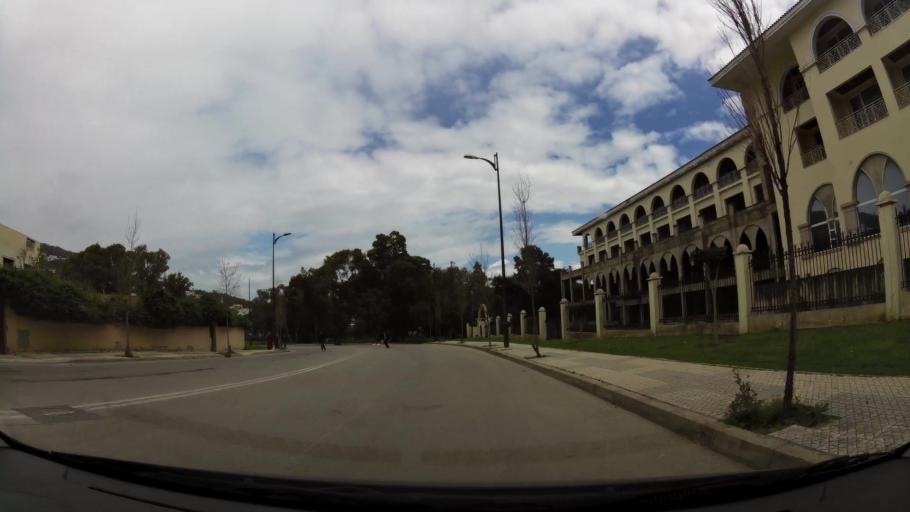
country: MA
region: Tanger-Tetouan
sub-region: Tanger-Assilah
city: Tangier
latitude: 35.7740
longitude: -5.8571
